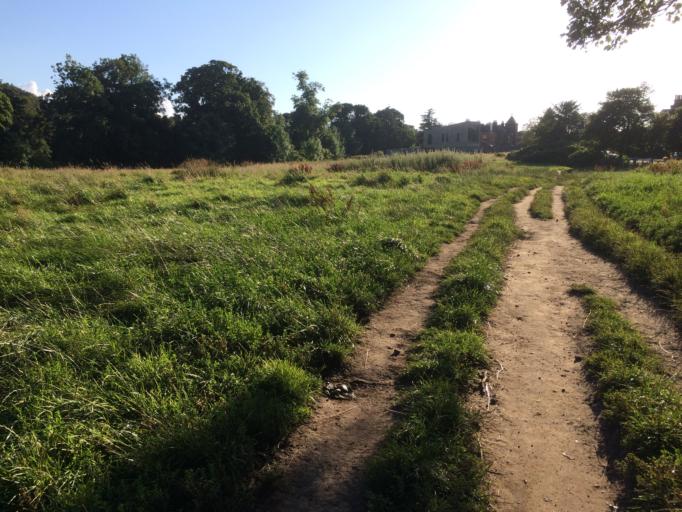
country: GB
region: Scotland
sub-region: Edinburgh
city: Edinburgh
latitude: 55.9212
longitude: -3.1977
